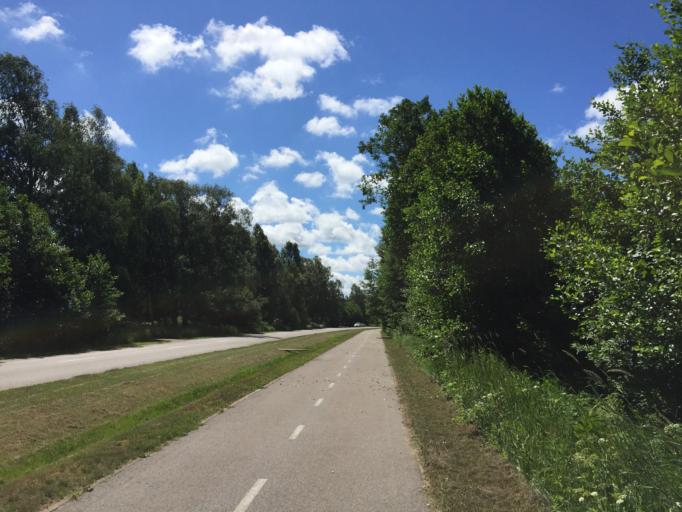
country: LV
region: Ventspils
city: Ventspils
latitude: 57.4353
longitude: 21.6542
